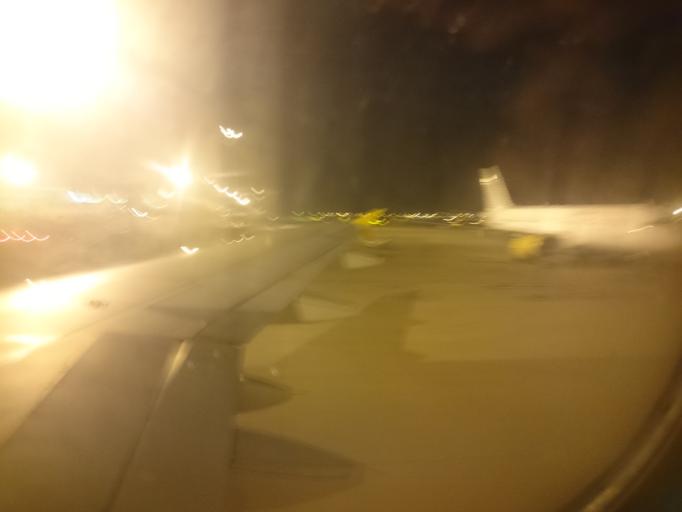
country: ES
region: Catalonia
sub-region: Provincia de Barcelona
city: El Prat de Llobregat
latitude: 41.2935
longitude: 2.0787
